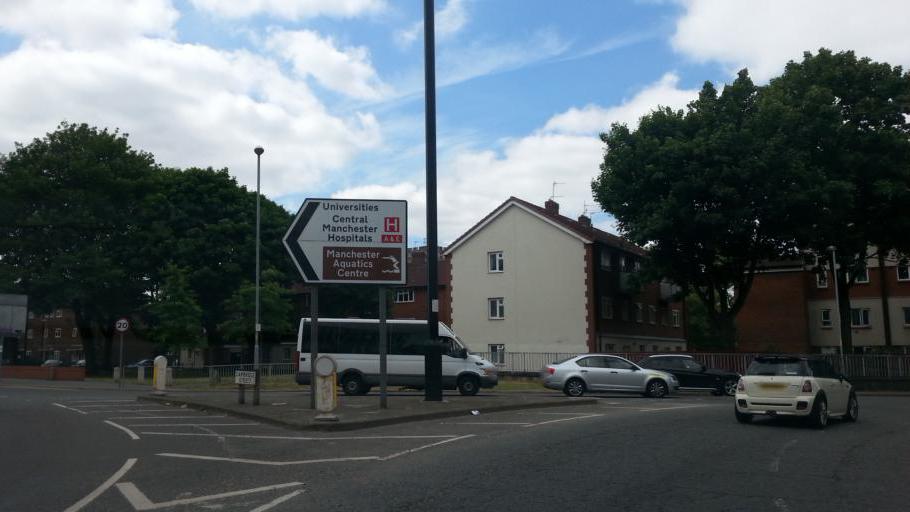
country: GB
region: England
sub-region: Manchester
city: Hulme
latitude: 53.4702
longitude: -2.2413
